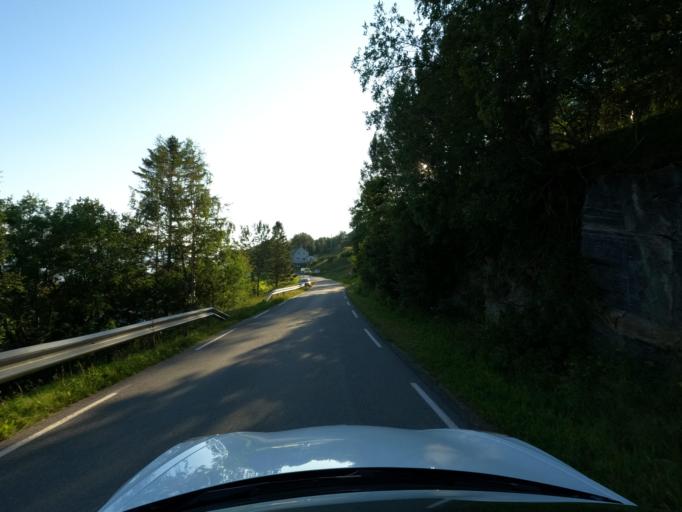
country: NO
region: Nordland
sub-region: Ballangen
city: Ballangen
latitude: 68.4698
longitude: 16.8630
